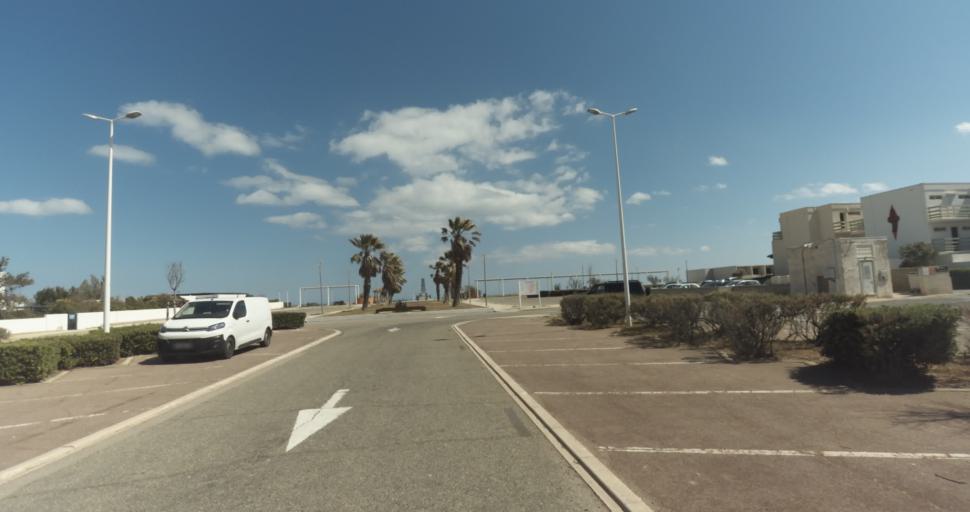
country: FR
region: Languedoc-Roussillon
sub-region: Departement de l'Aude
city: Leucate
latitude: 42.8634
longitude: 3.0446
